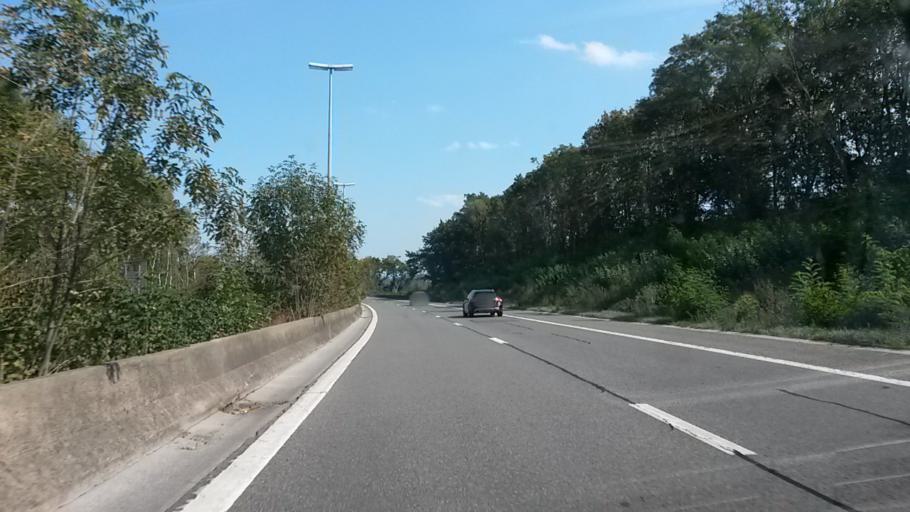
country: BE
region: Wallonia
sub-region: Province du Hainaut
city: Chatelet
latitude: 50.3881
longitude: 4.5028
